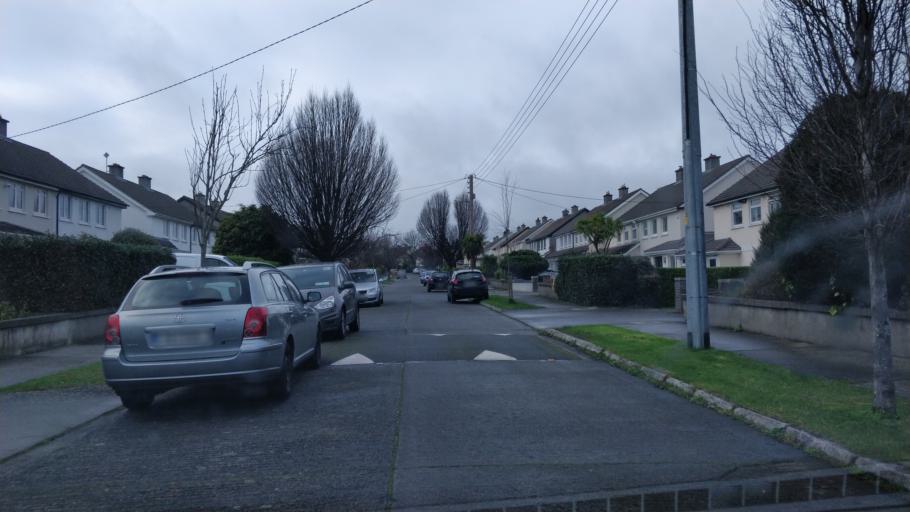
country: IE
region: Leinster
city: Foxrock
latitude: 53.2808
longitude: -6.1729
